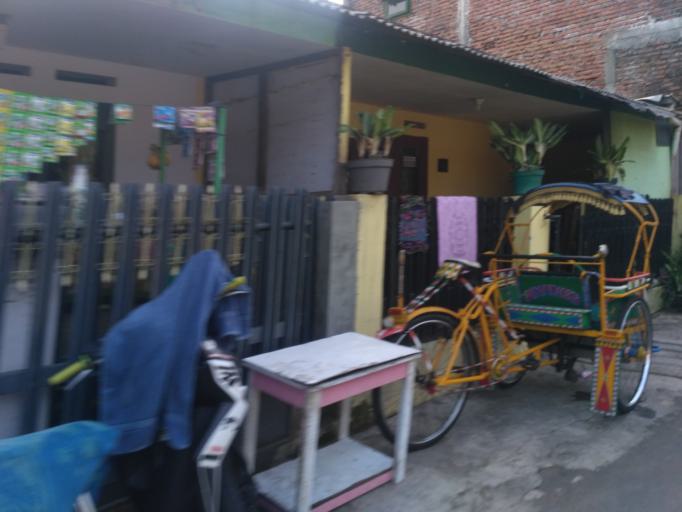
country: ID
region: East Java
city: Malang
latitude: -7.9597
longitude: 112.6274
